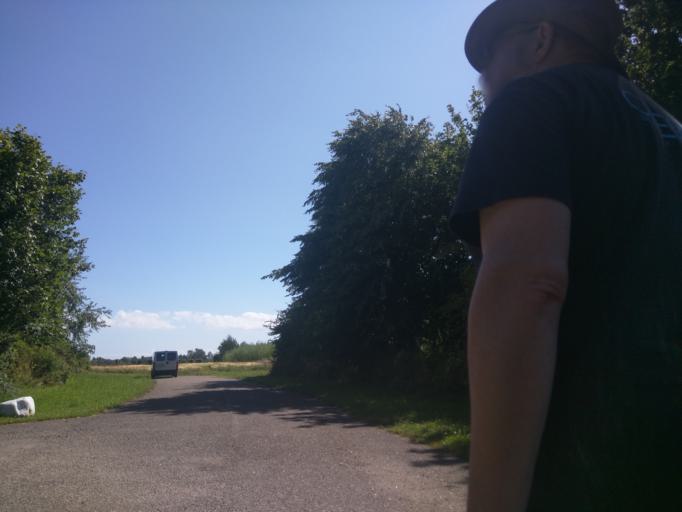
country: DK
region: Zealand
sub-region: Kalundborg Kommune
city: Svebolle
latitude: 55.6924
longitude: 11.2688
